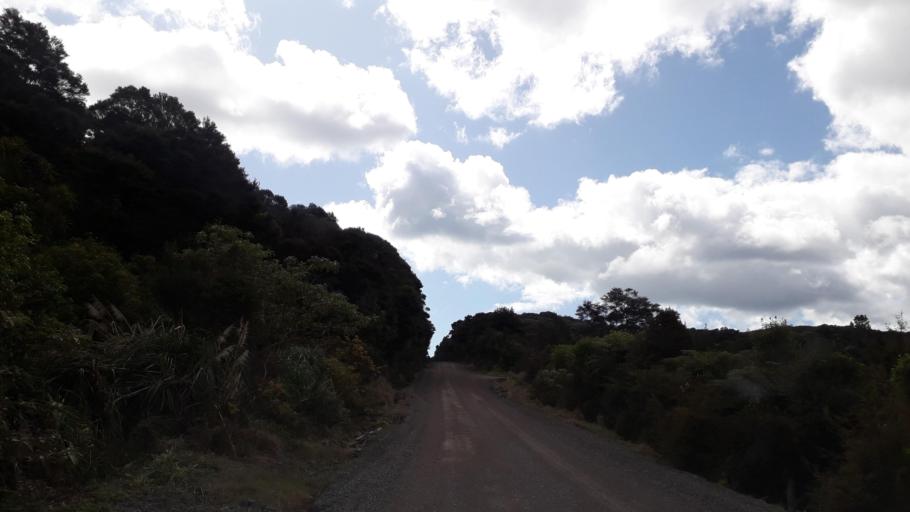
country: NZ
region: Northland
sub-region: Far North District
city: Paihia
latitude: -35.3330
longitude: 174.2325
